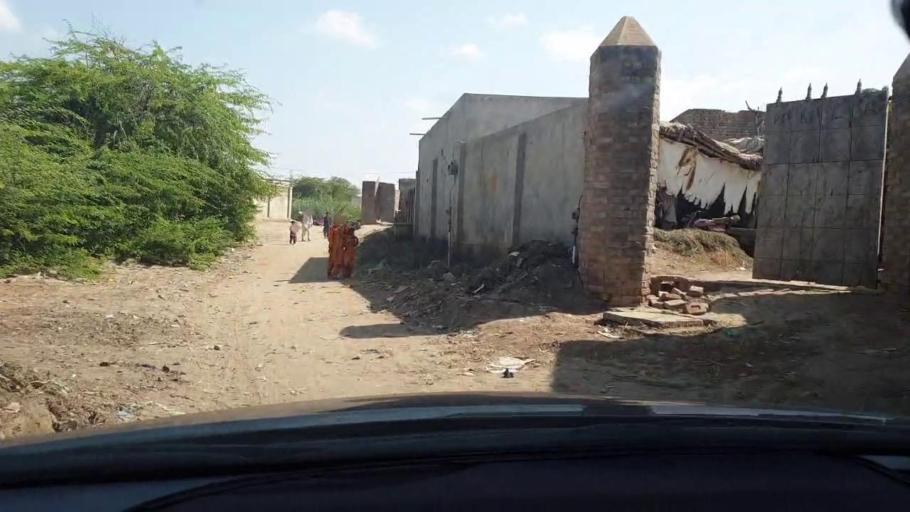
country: PK
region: Sindh
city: Naukot
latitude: 24.8738
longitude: 69.2592
